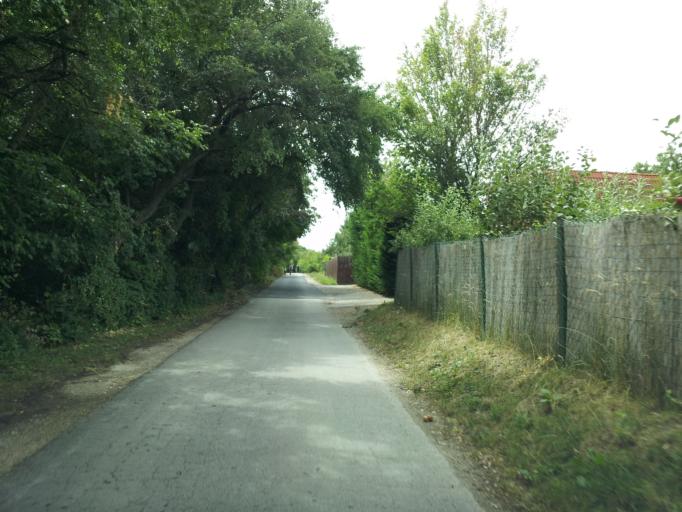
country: HU
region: Veszprem
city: Balatonkenese
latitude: 47.0001
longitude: 18.1694
